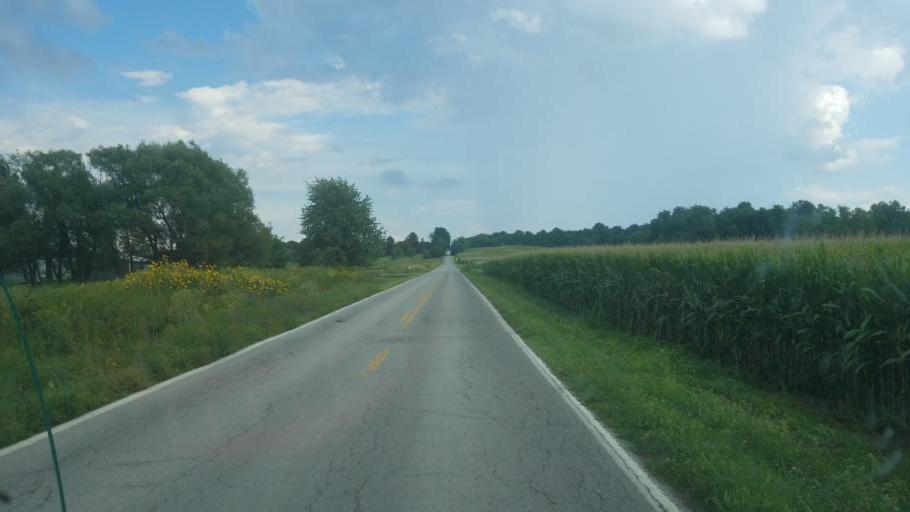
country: US
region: Ohio
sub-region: Huron County
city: Plymouth
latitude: 40.9955
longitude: -82.7098
